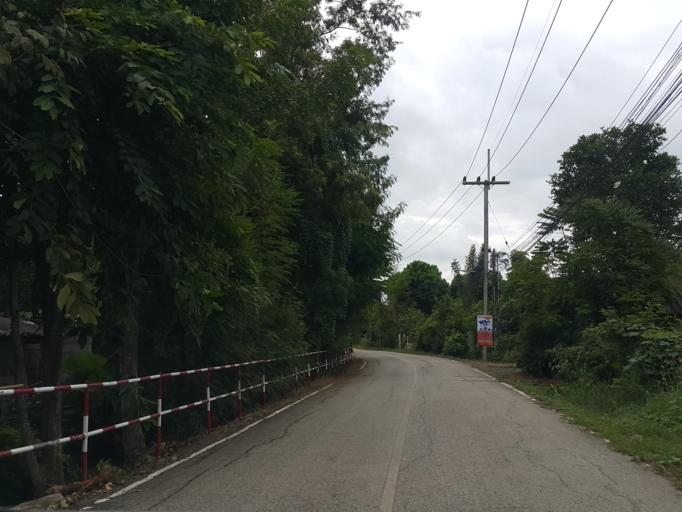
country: TH
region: Chiang Mai
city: San Kamphaeng
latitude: 18.7962
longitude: 99.1406
